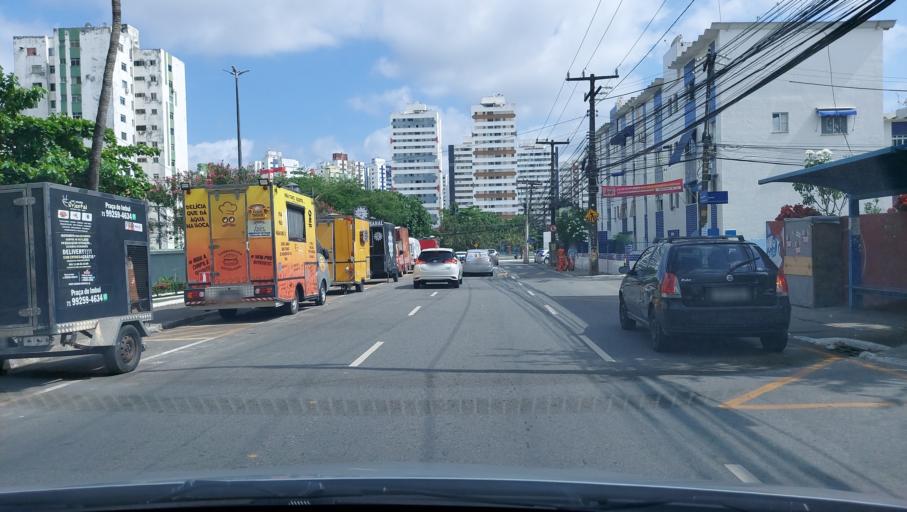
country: BR
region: Bahia
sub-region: Salvador
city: Salvador
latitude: -12.9708
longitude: -38.4349
